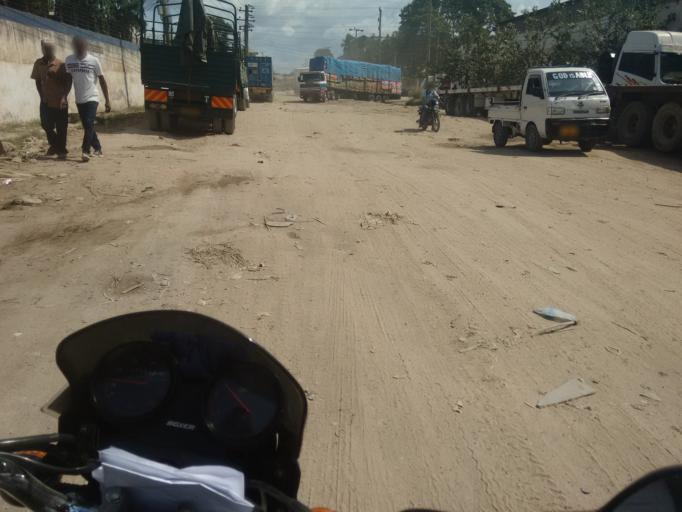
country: TZ
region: Dar es Salaam
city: Dar es Salaam
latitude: -6.8470
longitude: 39.2562
